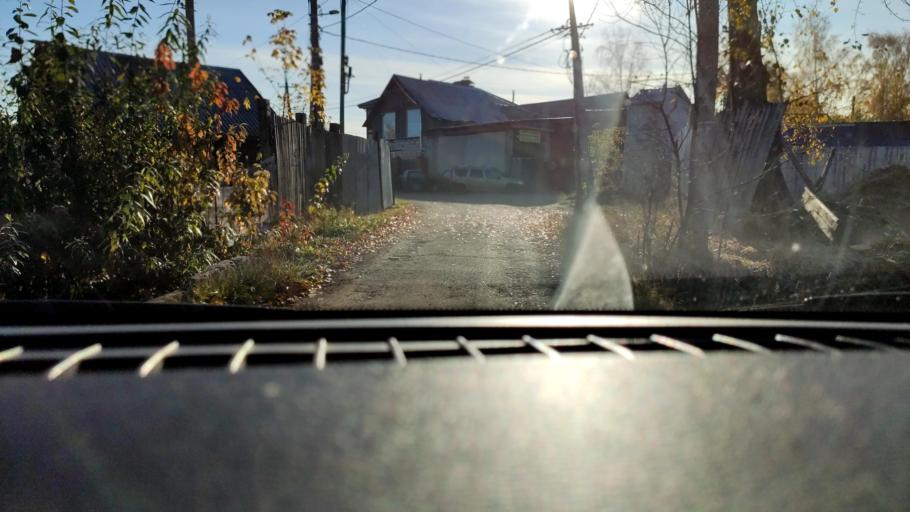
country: RU
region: Perm
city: Perm
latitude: 58.0287
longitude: 56.2119
